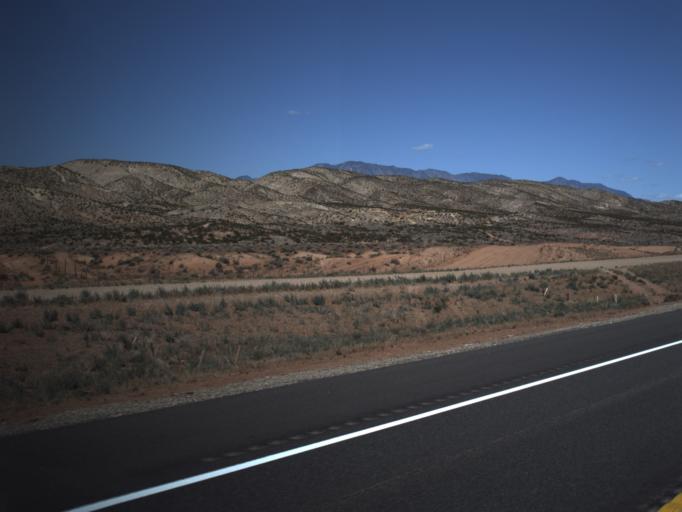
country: US
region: Utah
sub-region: Washington County
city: Washington
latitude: 37.0839
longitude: -113.4778
